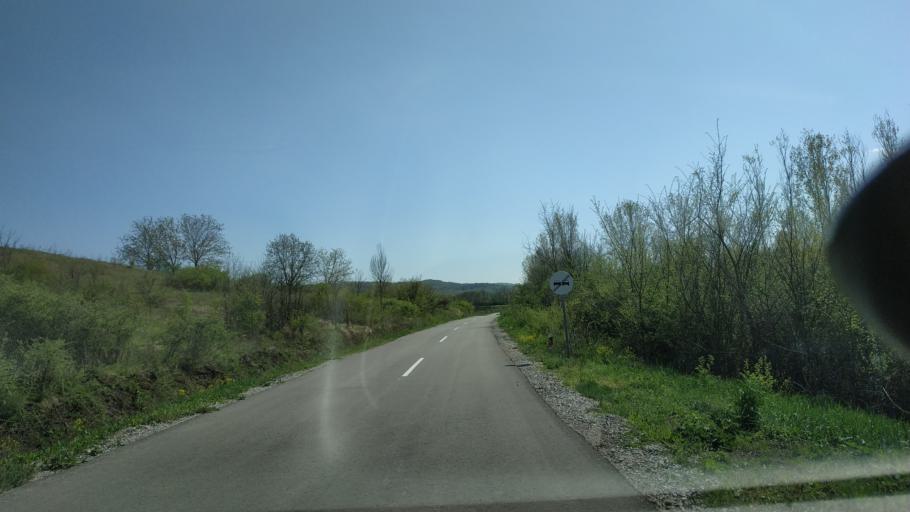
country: RS
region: Central Serbia
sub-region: Nisavski Okrug
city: Nis
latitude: 43.4774
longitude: 21.8684
